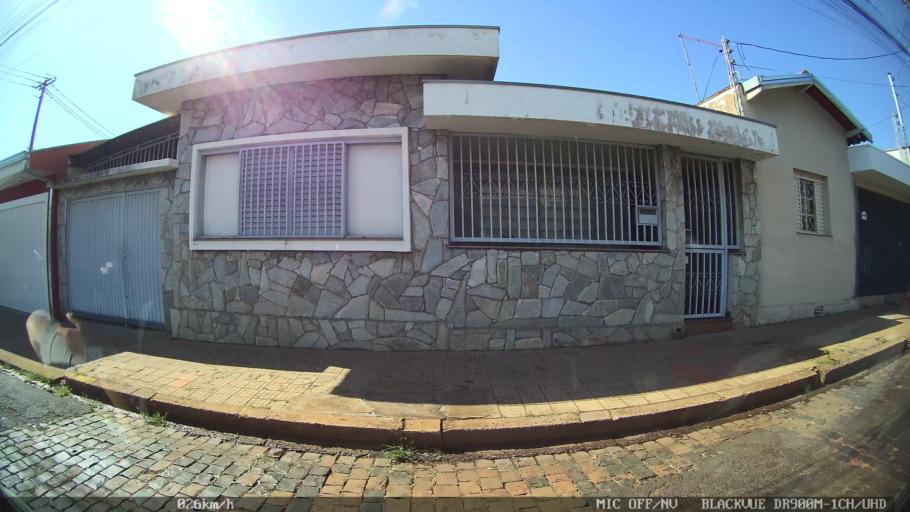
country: BR
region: Sao Paulo
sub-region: Batatais
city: Batatais
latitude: -20.8975
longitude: -47.5839
